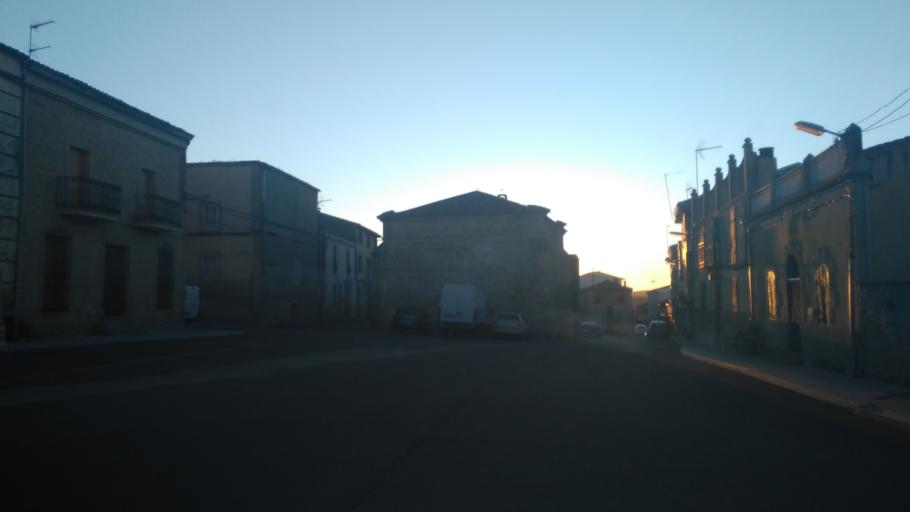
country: ES
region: Castille and Leon
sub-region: Provincia de Salamanca
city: Aldeadavila de la Ribera
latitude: 41.2178
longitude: -6.6156
